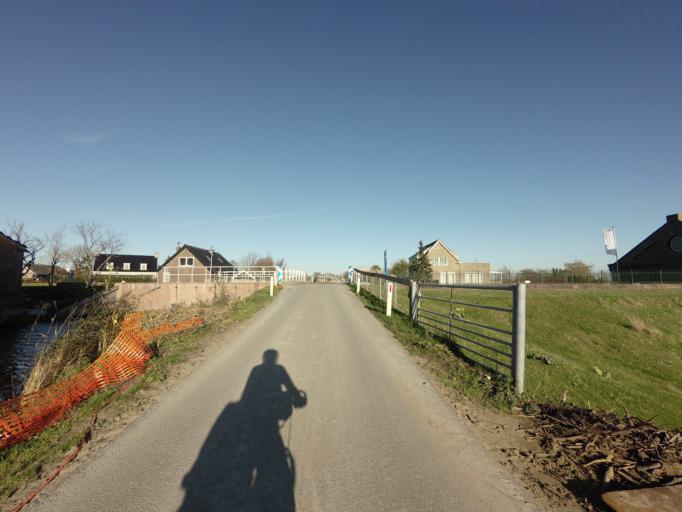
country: NL
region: South Holland
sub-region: Gemeente Nieuwkoop
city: Nieuwkoop
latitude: 52.1595
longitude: 4.7273
